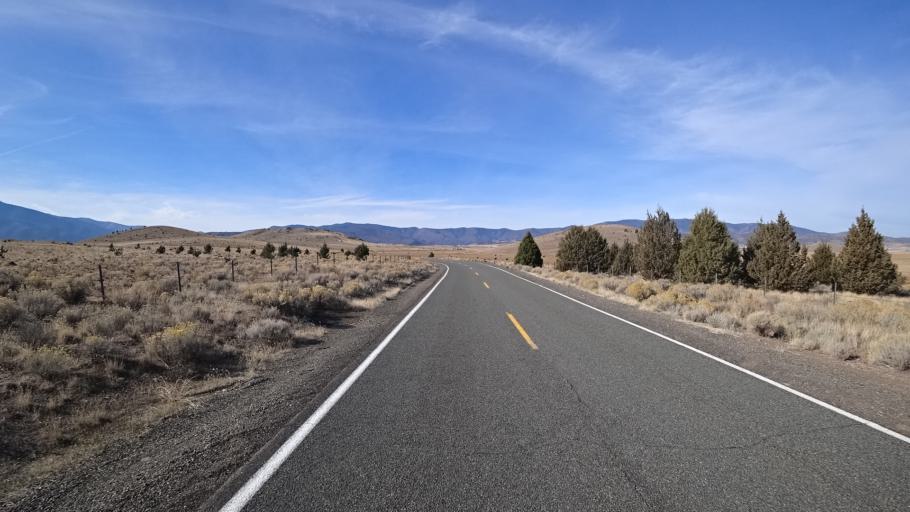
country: US
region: California
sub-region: Siskiyou County
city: Weed
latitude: 41.5511
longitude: -122.4890
